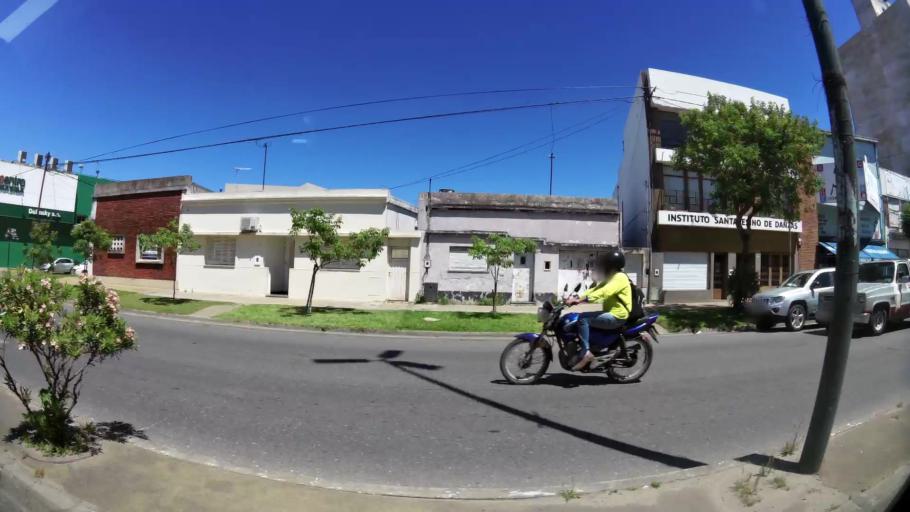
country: AR
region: Santa Fe
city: Santa Fe de la Vera Cruz
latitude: -31.6221
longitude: -60.7054
